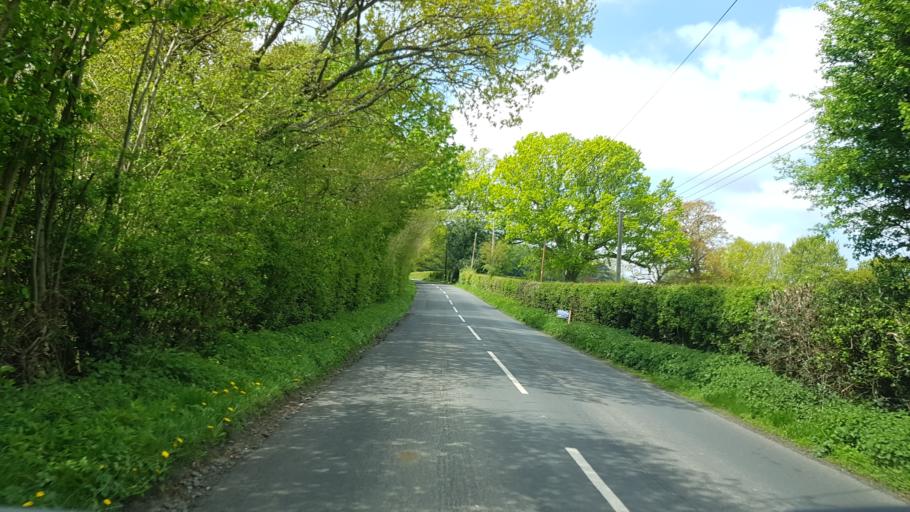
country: GB
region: England
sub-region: East Sussex
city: Robertsbridge
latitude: 51.0315
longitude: 0.4464
